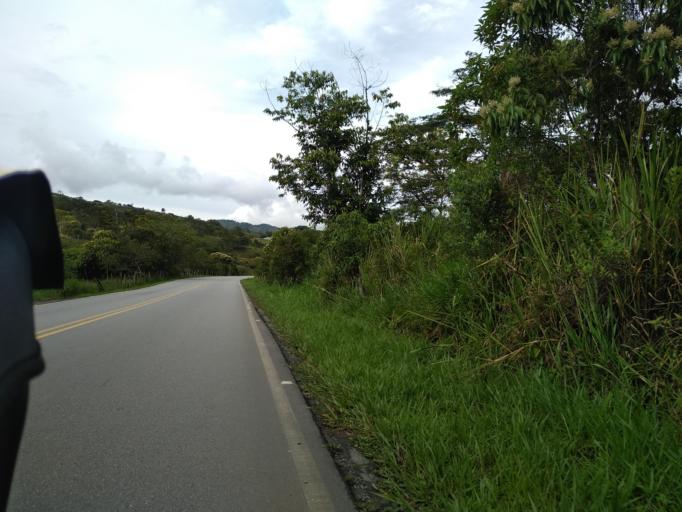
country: CO
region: Santander
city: Suaita
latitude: 6.1089
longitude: -73.3666
